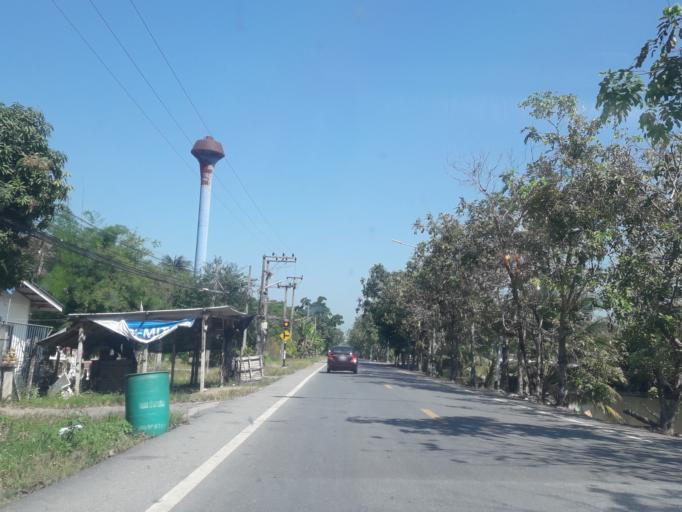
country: TH
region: Pathum Thani
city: Nong Suea
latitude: 14.1794
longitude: 100.8458
